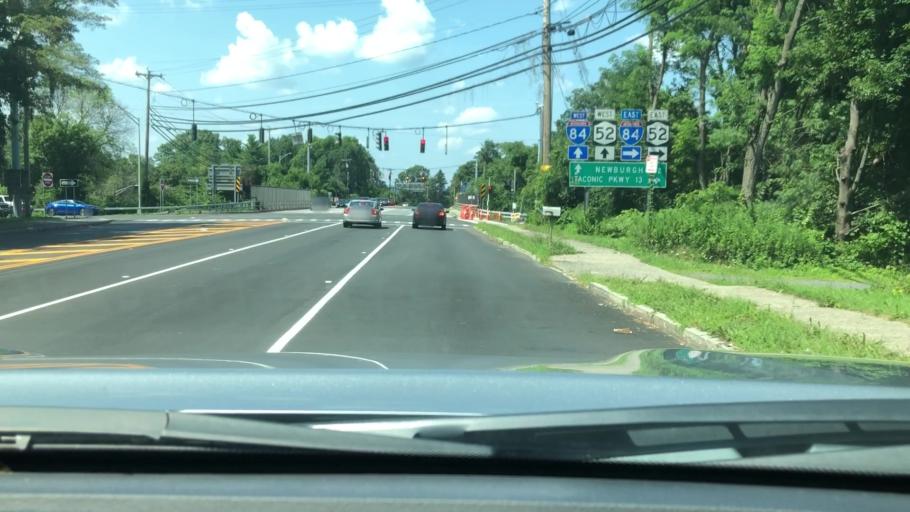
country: US
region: New York
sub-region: Dutchess County
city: Beacon
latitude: 41.5169
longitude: -73.9733
